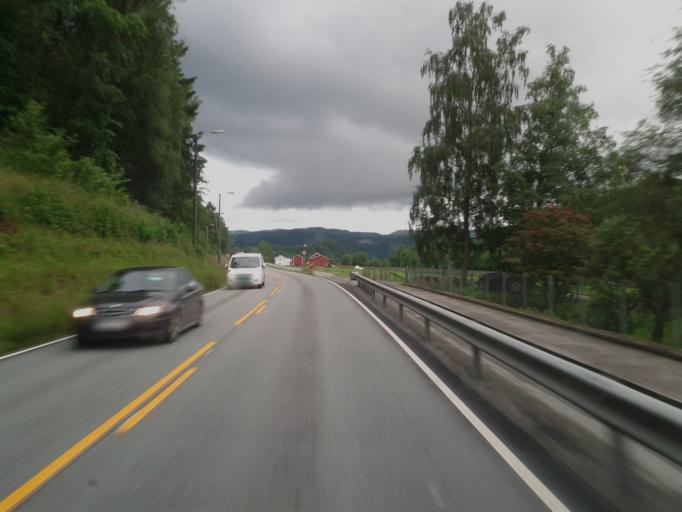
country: NO
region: Sor-Trondelag
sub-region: Melhus
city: Lundamo
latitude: 63.1297
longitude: 10.2457
